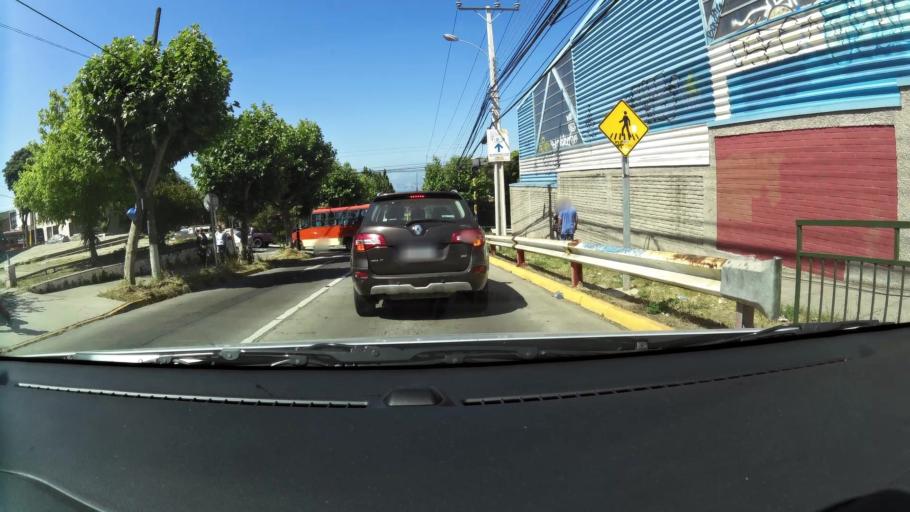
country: CL
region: Valparaiso
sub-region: Provincia de Valparaiso
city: Valparaiso
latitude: -33.0308
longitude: -71.6376
